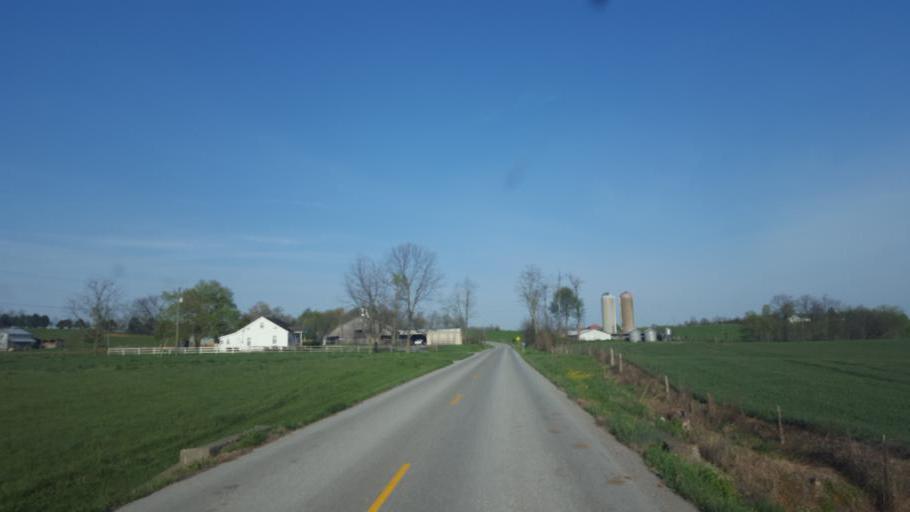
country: US
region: Kentucky
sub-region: Hardin County
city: Elizabethtown
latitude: 37.5008
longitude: -85.9347
